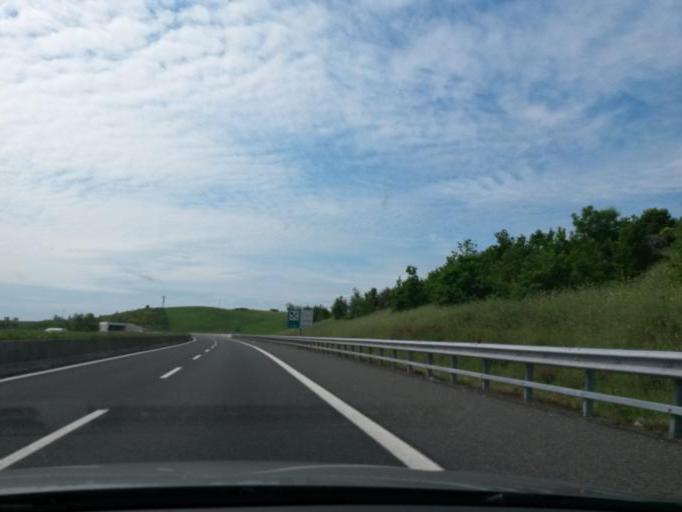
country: IT
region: Tuscany
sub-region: Province of Pisa
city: Orciano Pisano
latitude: 43.5085
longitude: 10.4735
